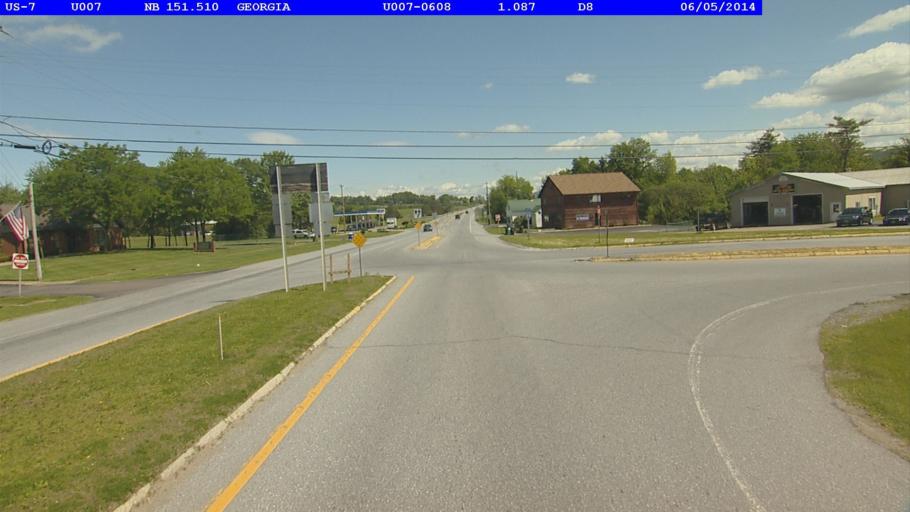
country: US
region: Vermont
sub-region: Chittenden County
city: Milton
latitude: 44.6946
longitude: -73.1078
